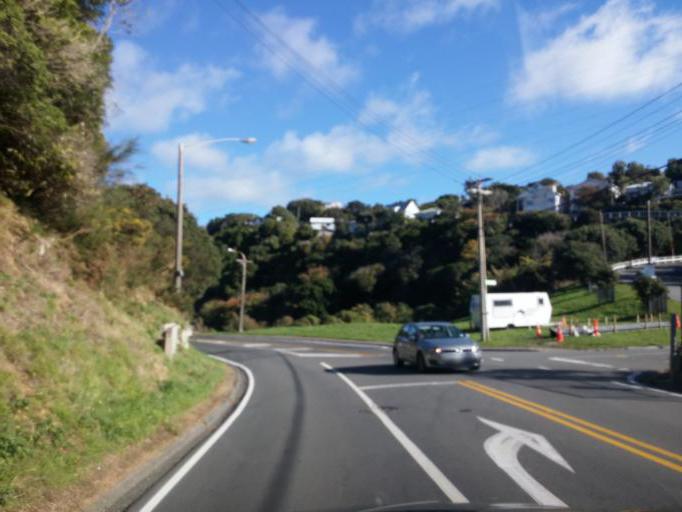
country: NZ
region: Wellington
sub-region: Wellington City
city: Kelburn
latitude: -41.2798
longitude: 174.7544
